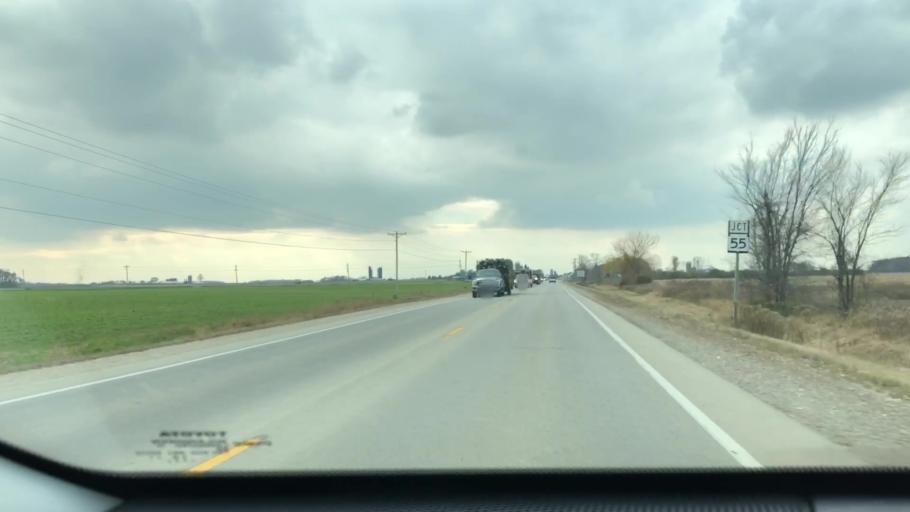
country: US
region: Wisconsin
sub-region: Outagamie County
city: Seymour
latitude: 44.5006
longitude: -88.2851
